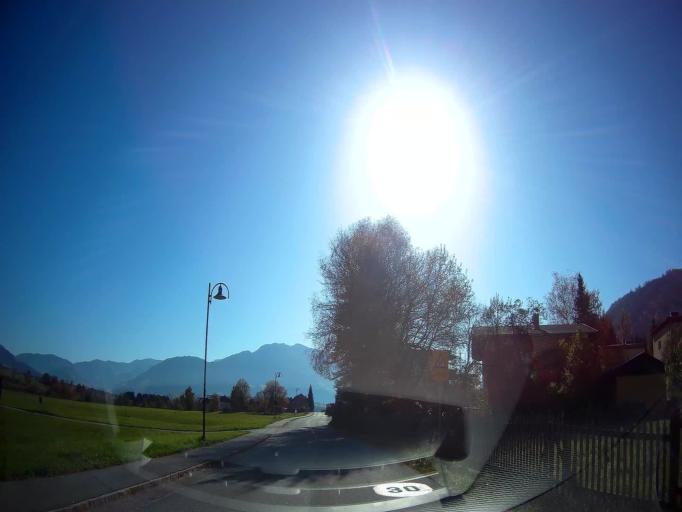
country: AT
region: Salzburg
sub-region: Politischer Bezirk Zell am See
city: Saalfelden am Steinernen Meer
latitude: 47.4426
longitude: 12.8181
